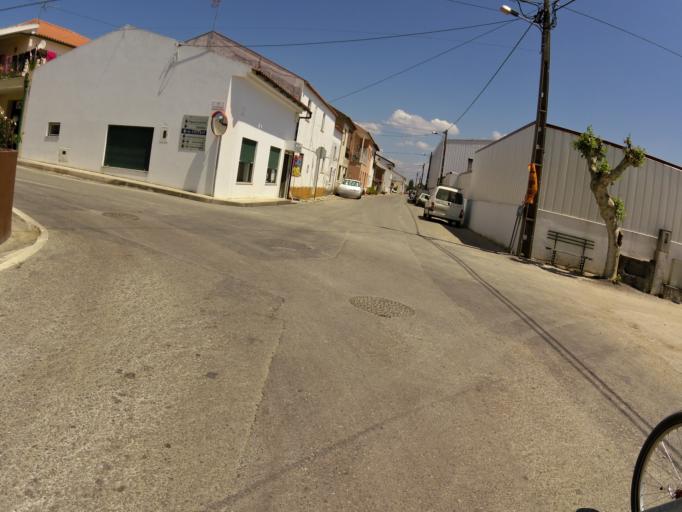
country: PT
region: Coimbra
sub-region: Montemor-O-Velho
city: Montemor-o-Velho
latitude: 40.1521
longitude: -8.7091
